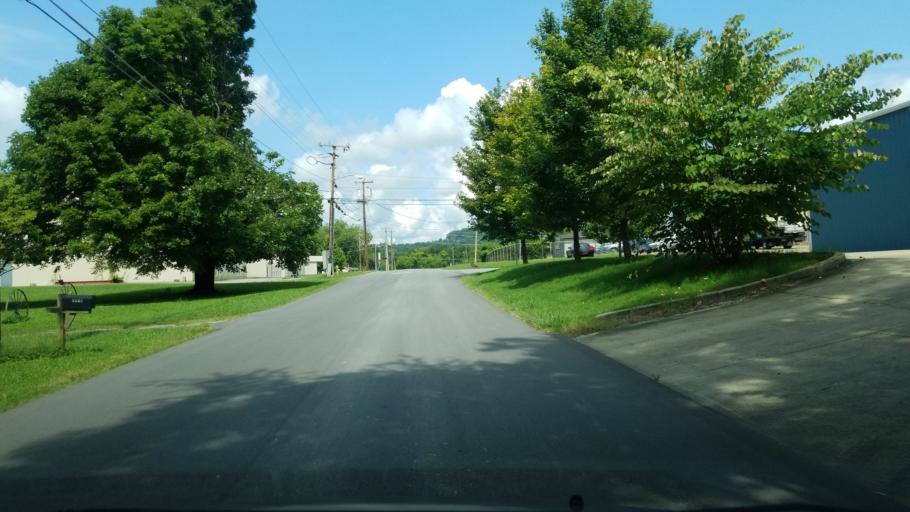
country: US
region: Tennessee
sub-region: Hamilton County
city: East Chattanooga
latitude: 35.0723
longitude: -85.2659
